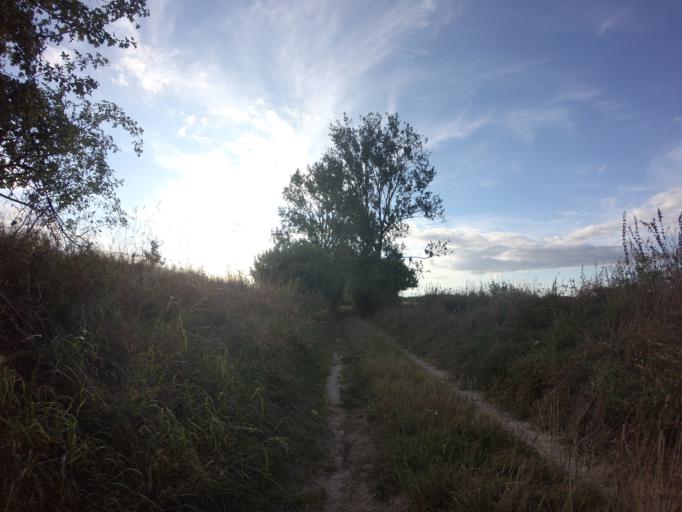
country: PL
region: West Pomeranian Voivodeship
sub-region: Powiat choszczenski
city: Choszczno
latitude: 53.1169
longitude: 15.4266
